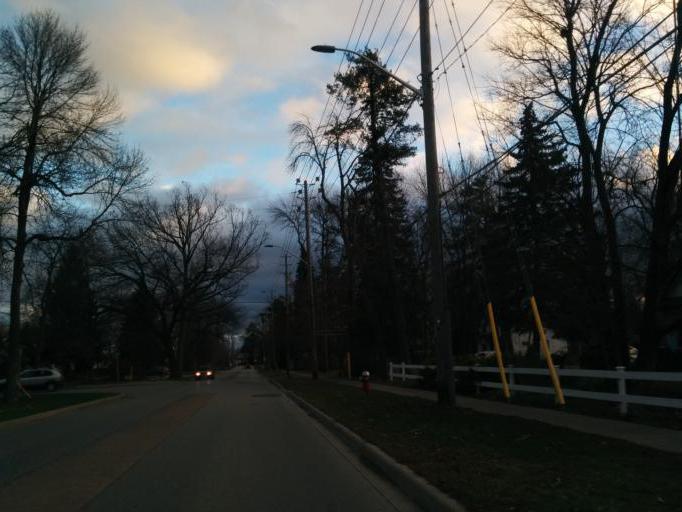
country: CA
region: Ontario
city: Mississauga
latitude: 43.5229
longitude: -79.6316
